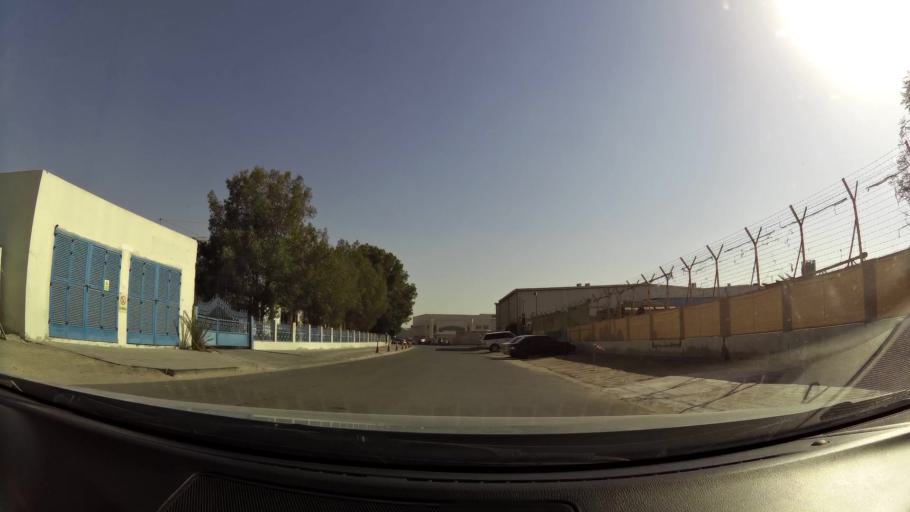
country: AE
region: Dubai
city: Dubai
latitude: 24.9892
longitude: 55.1062
